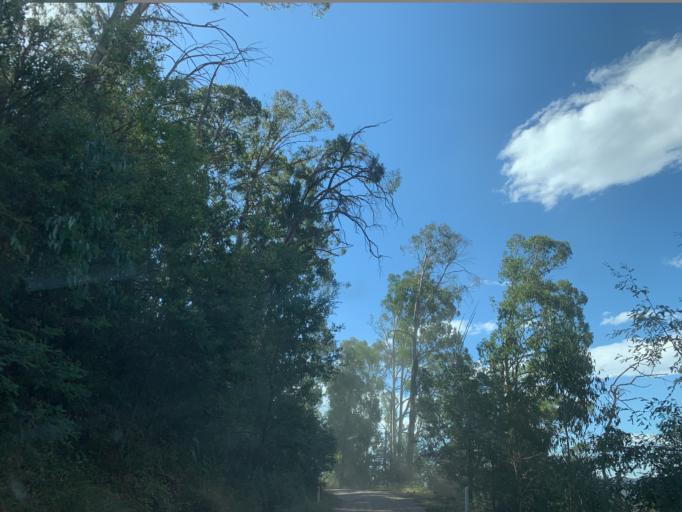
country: AU
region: Victoria
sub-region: Mansfield
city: Mansfield
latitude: -37.1002
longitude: 146.5100
